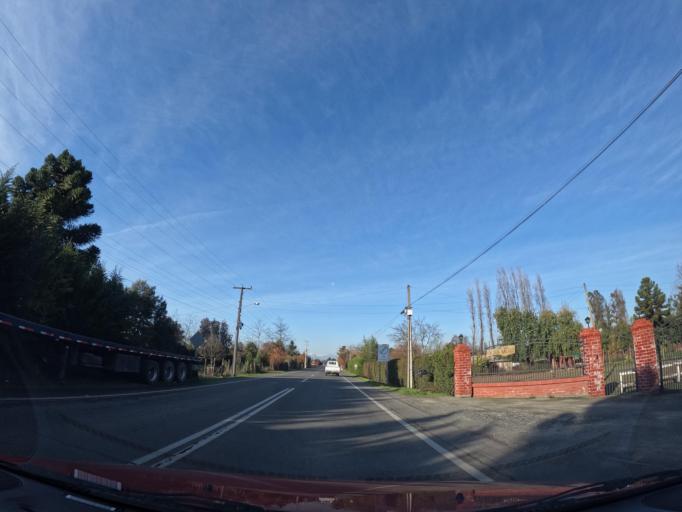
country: CL
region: Maule
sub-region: Provincia de Talca
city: San Clemente
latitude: -35.6230
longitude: -71.4976
